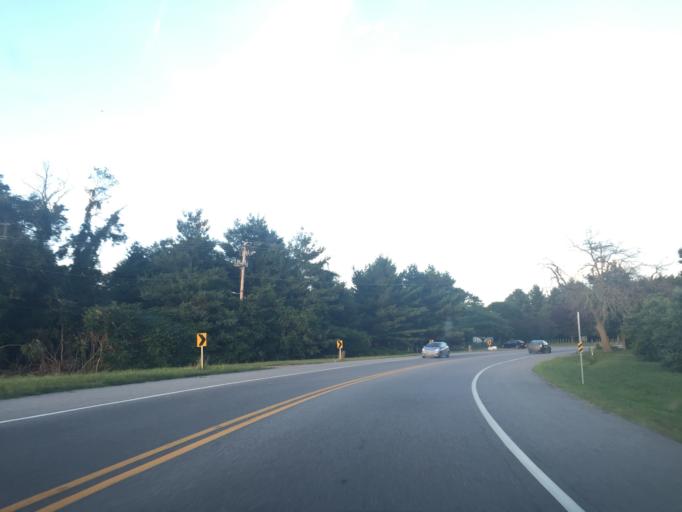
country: US
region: Delaware
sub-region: New Castle County
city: Middletown
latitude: 39.4583
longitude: -75.6647
